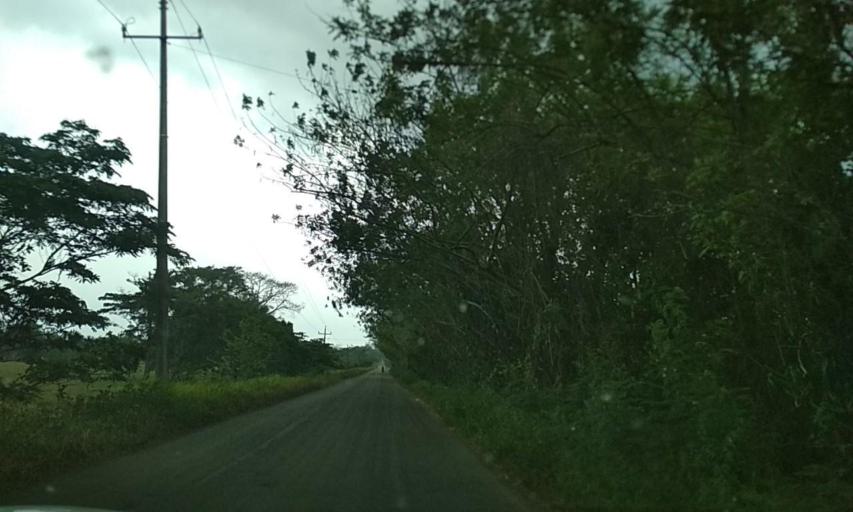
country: MX
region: Tabasco
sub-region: Huimanguillo
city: Francisco Rueda
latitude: 17.5599
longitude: -94.1181
